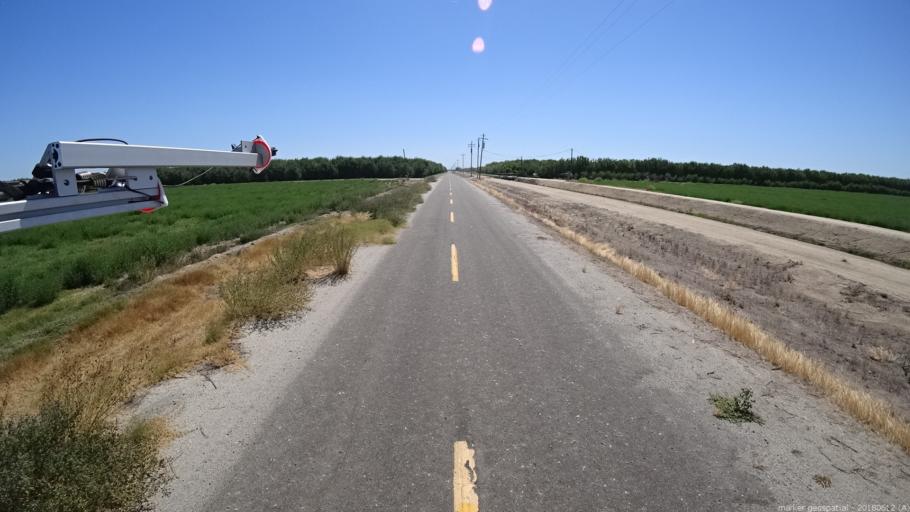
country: US
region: California
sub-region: Madera County
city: Chowchilla
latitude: 37.0255
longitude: -120.2890
